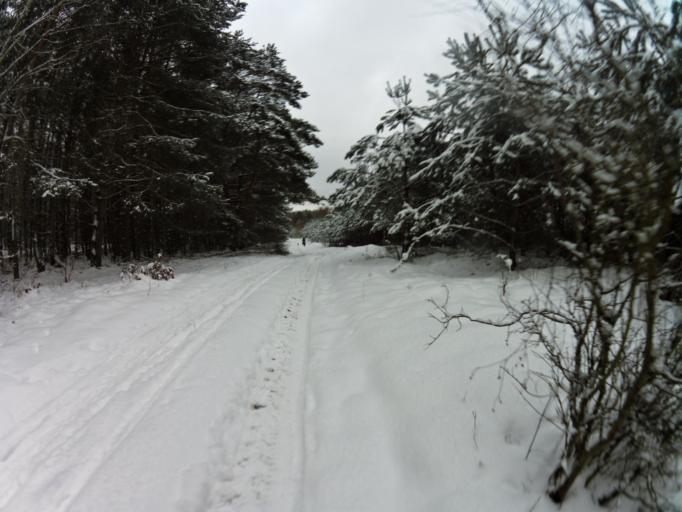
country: PL
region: West Pomeranian Voivodeship
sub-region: Powiat stargardzki
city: Dobrzany
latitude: 53.3571
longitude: 15.5142
